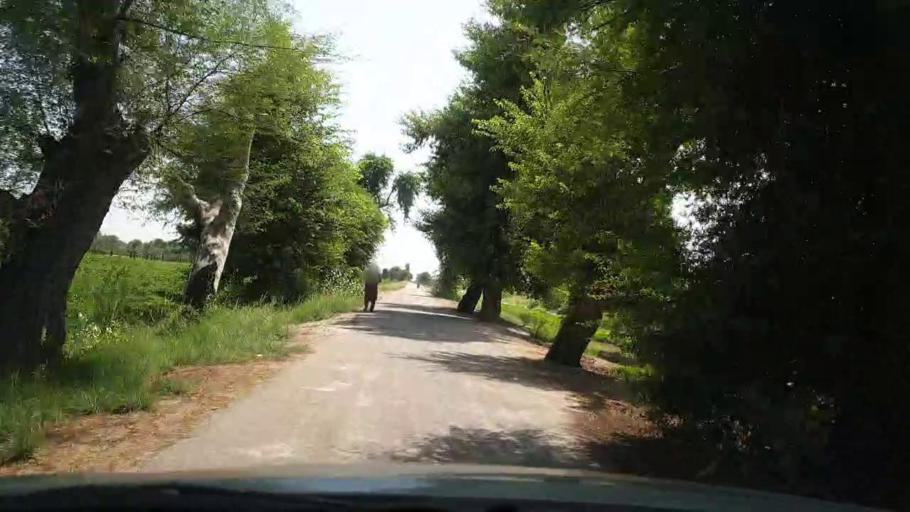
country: PK
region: Sindh
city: Pano Aqil
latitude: 27.7375
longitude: 69.0986
